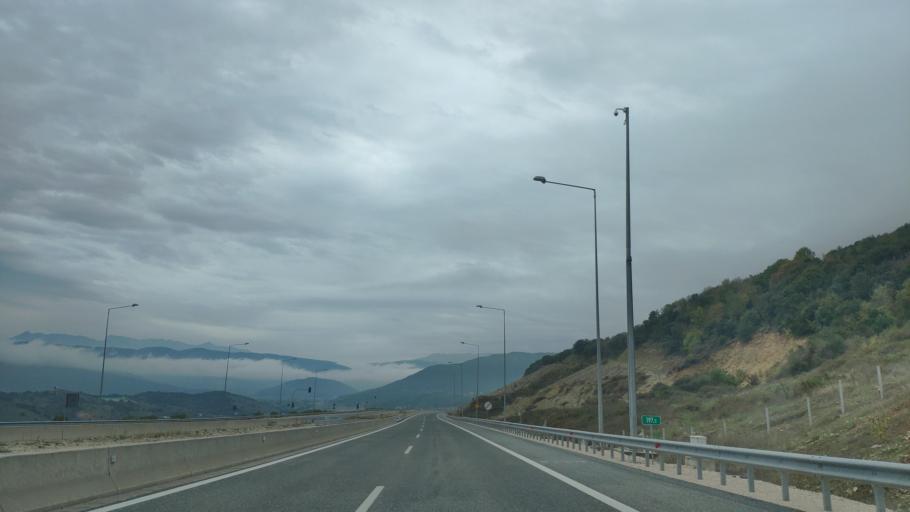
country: GR
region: Epirus
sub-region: Nomos Ioanninon
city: Pedini
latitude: 39.5608
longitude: 20.8297
